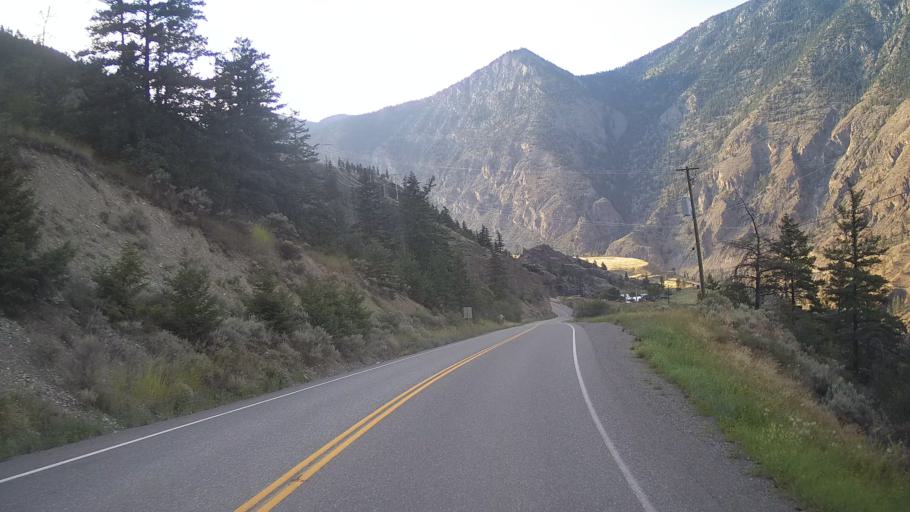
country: CA
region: British Columbia
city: Lillooet
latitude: 50.7456
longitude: -121.8909
